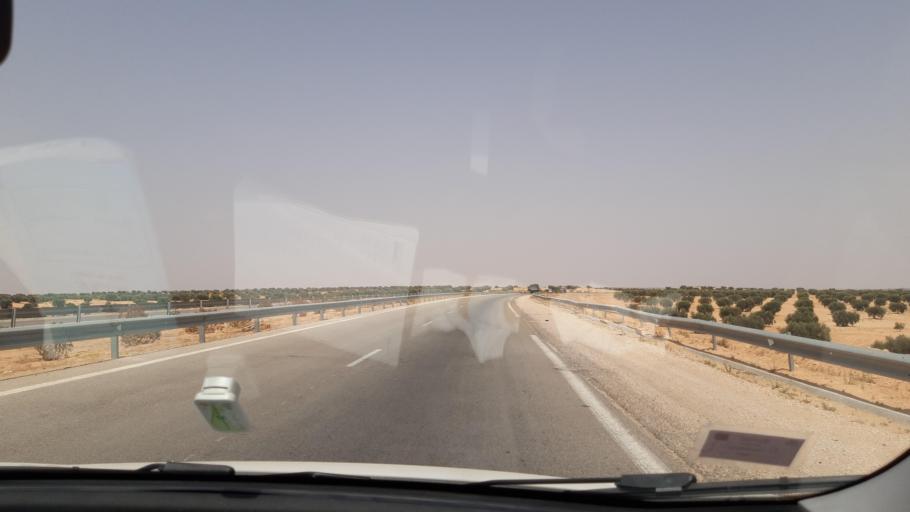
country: TN
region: Safaqis
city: Bi'r `Ali Bin Khalifah
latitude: 34.5218
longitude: 10.0797
